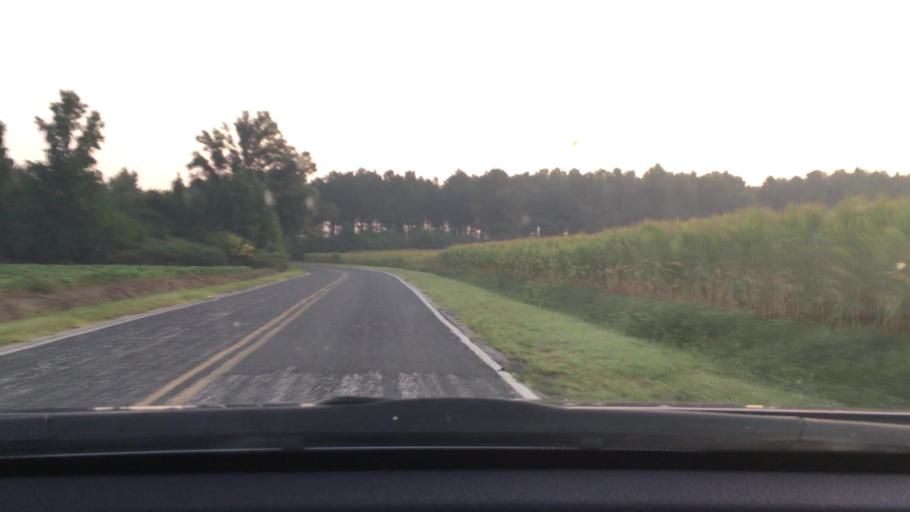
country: US
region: South Carolina
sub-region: Lee County
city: Bishopville
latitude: 34.2274
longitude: -80.1331
